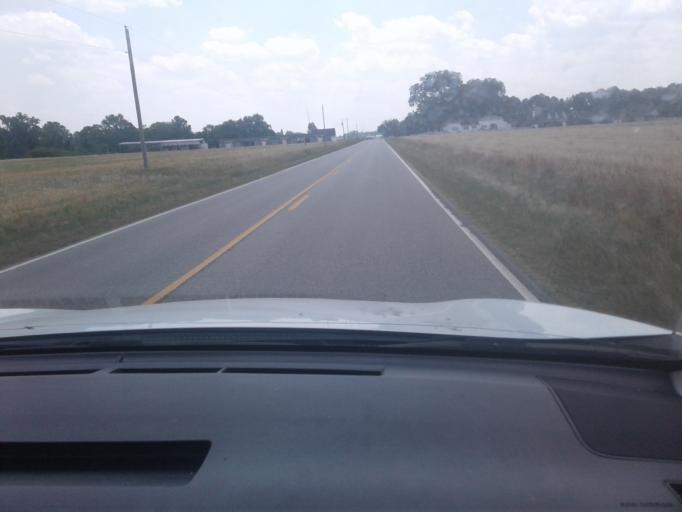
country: US
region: North Carolina
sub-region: Harnett County
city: Coats
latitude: 35.3678
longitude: -78.6317
